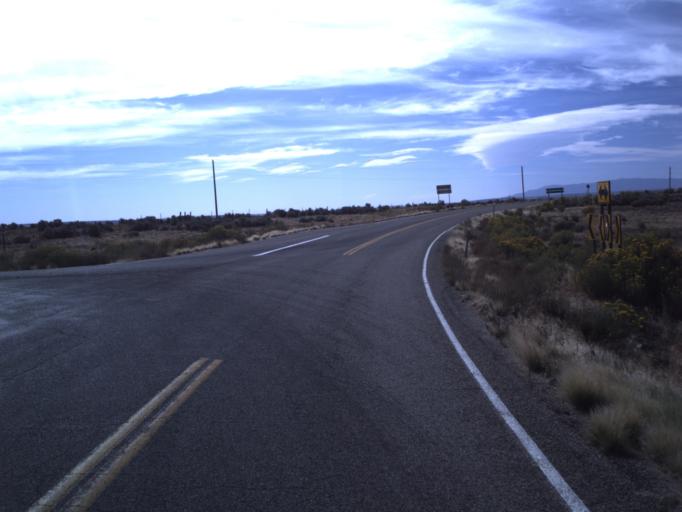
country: US
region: Utah
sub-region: San Juan County
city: Blanding
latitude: 37.4202
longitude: -109.3346
